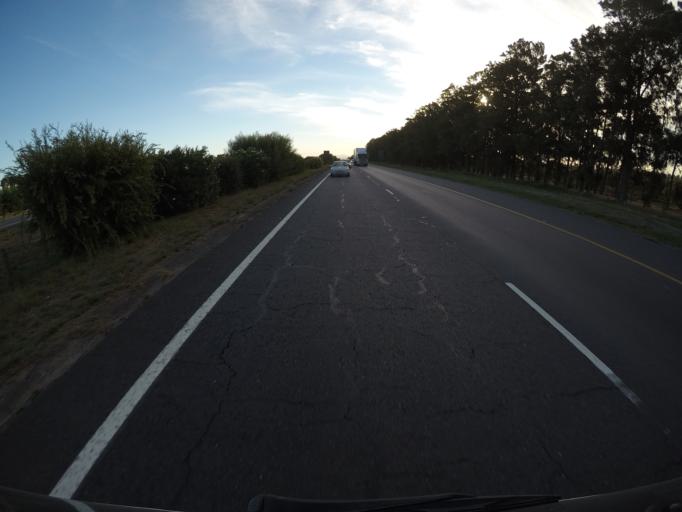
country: ZA
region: Western Cape
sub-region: City of Cape Town
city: Kraaifontein
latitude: -33.8241
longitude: 18.7760
